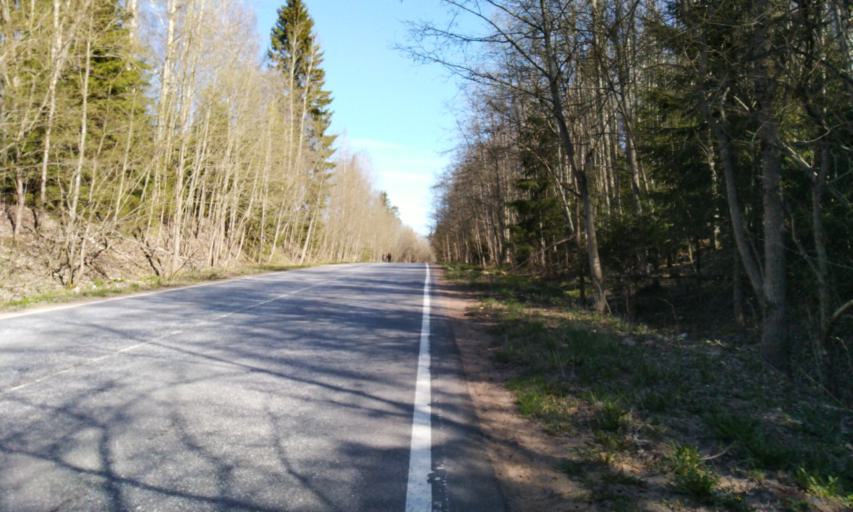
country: RU
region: Leningrad
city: Garbolovo
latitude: 60.3618
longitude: 30.4442
